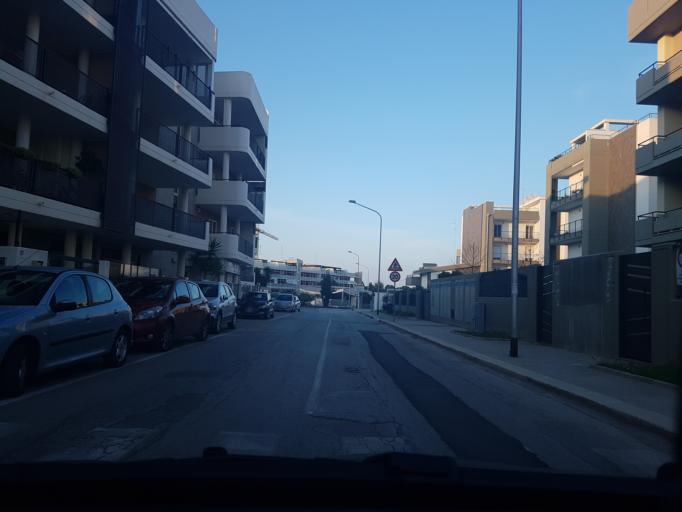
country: IT
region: Apulia
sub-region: Provincia di Bari
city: Bitritto
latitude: 41.0446
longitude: 16.8306
